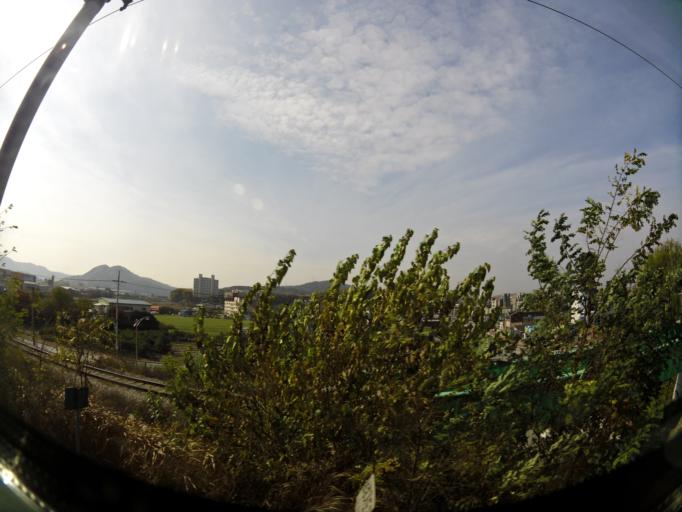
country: KR
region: Daejeon
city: Sintansin
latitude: 36.5275
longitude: 127.3733
